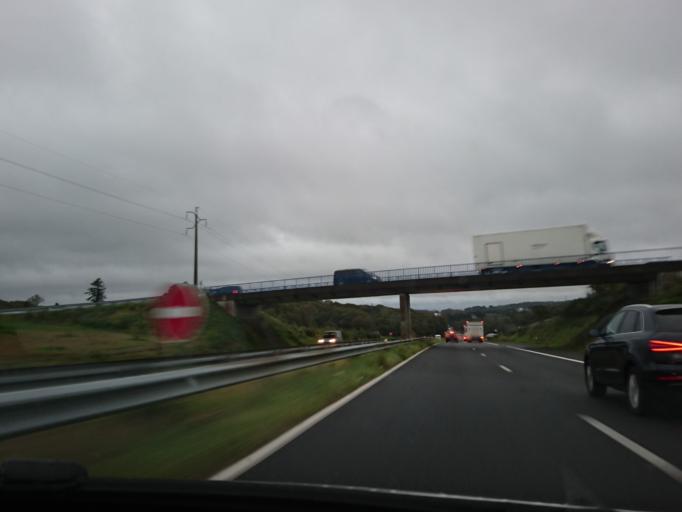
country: FR
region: Brittany
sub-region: Departement du Finistere
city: Loperhet
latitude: 48.3825
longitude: -4.3067
